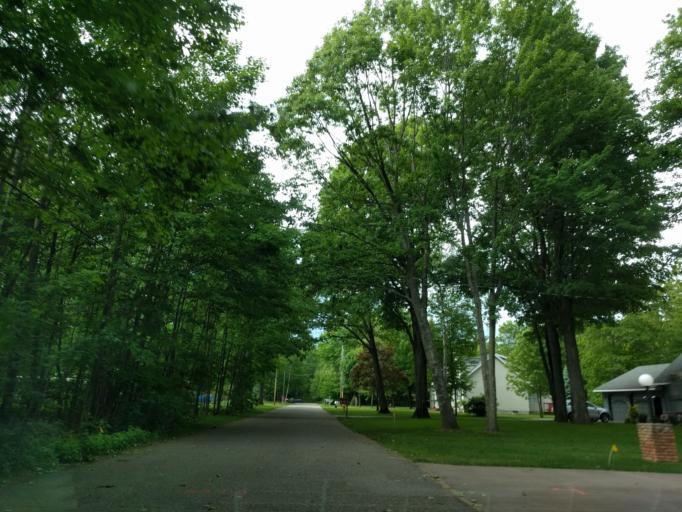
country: US
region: Michigan
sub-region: Marquette County
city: Trowbridge Park
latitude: 46.5634
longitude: -87.4428
